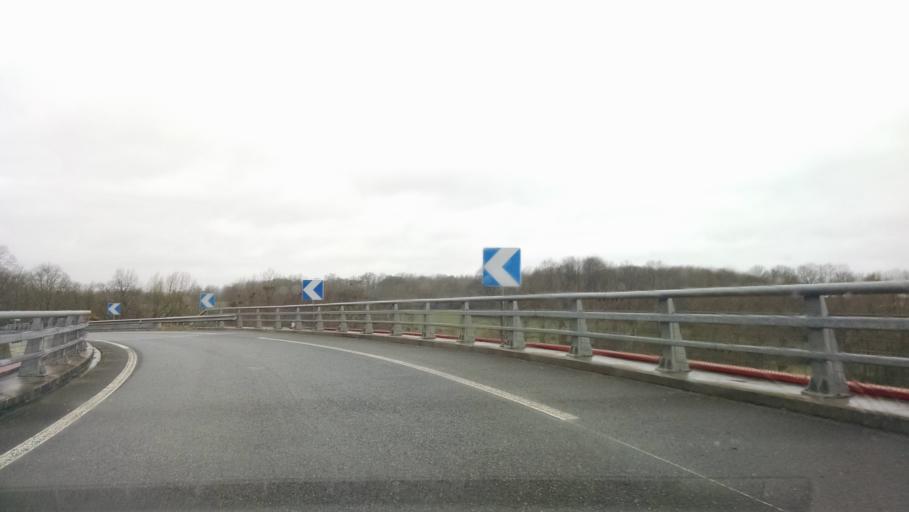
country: FR
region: Pays de la Loire
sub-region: Departement de la Loire-Atlantique
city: Clisson
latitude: 47.1010
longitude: -1.2838
